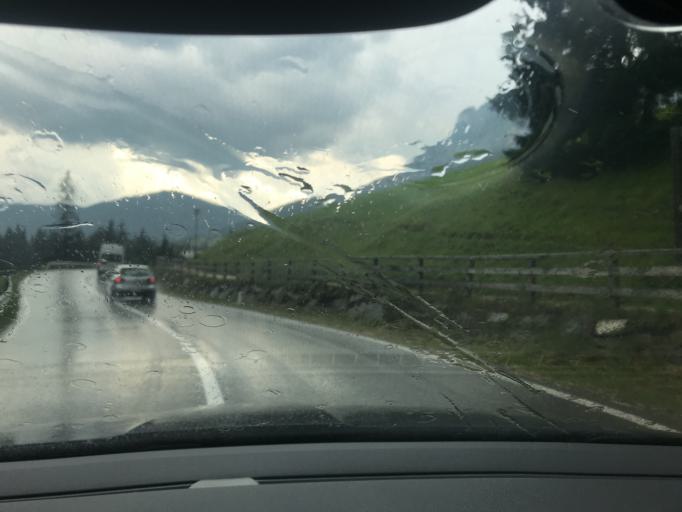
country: IT
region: Trentino-Alto Adige
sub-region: Bolzano
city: Badia
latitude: 46.6147
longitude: 11.8935
